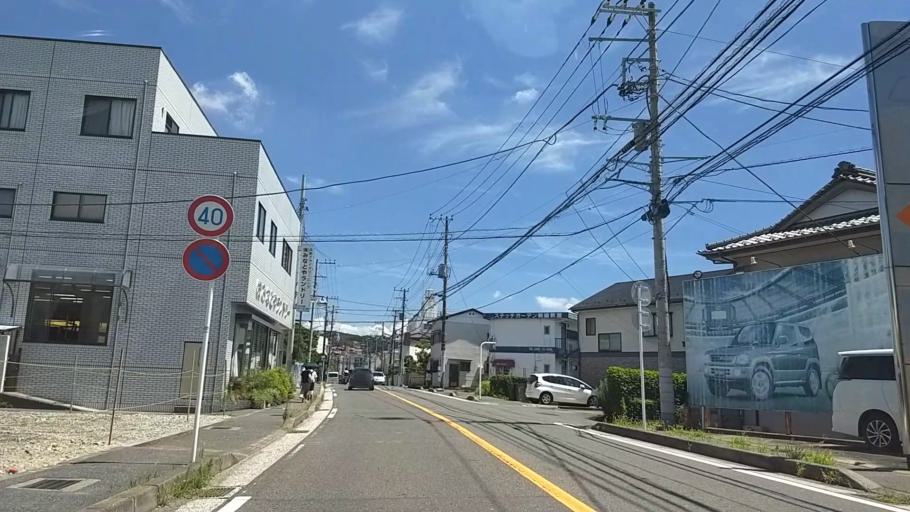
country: JP
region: Kanagawa
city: Zushi
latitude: 35.2984
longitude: 139.5721
